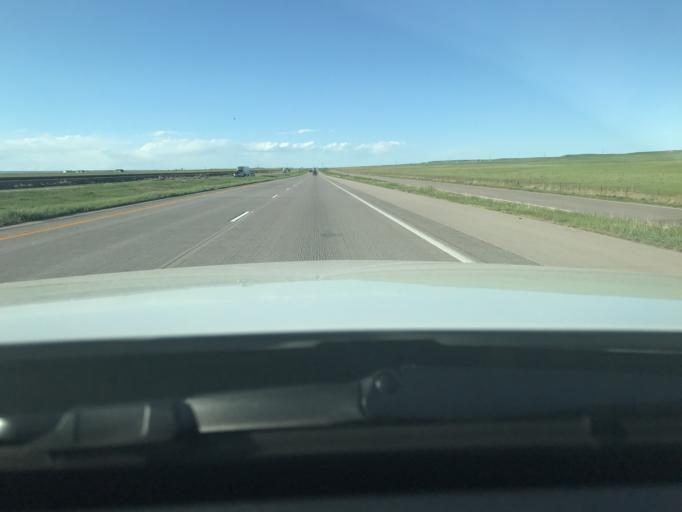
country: US
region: Colorado
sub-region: Larimer County
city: Wellington
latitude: 40.8000
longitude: -104.9795
